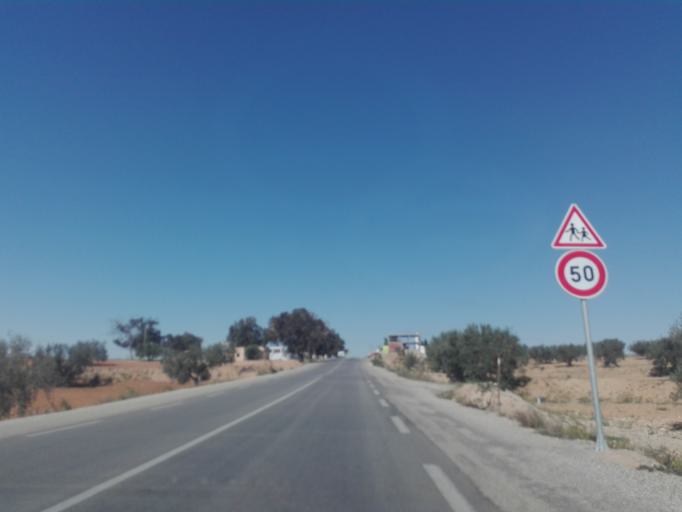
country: TN
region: Safaqis
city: Bi'r `Ali Bin Khalifah
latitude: 34.7413
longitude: 10.3748
